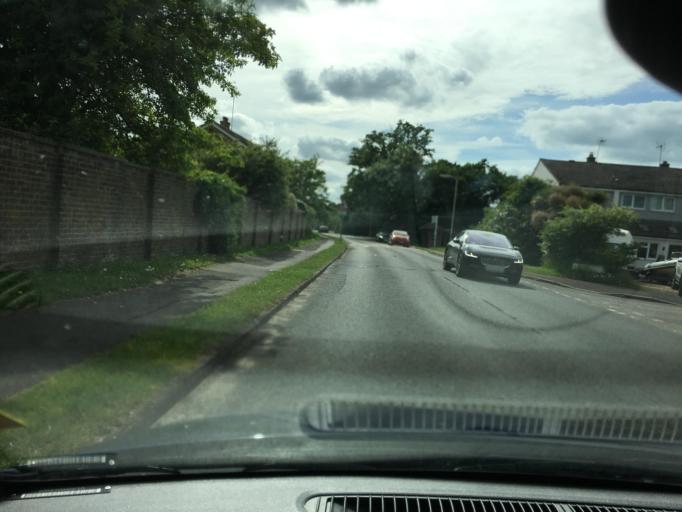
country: GB
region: England
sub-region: Hampshire
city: Yateley
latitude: 51.3409
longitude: -0.8436
